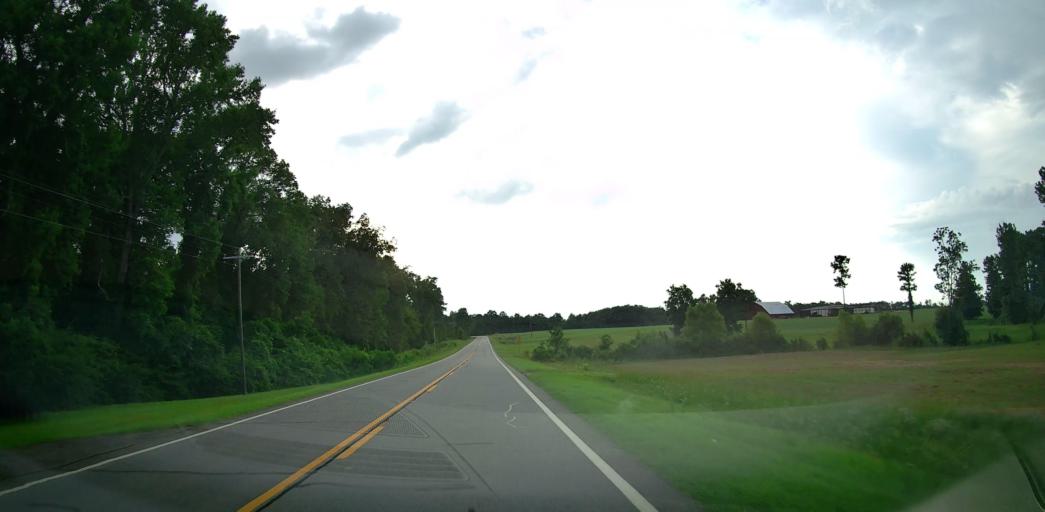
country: US
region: Georgia
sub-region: Pulaski County
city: Hawkinsville
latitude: 32.2935
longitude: -83.5171
